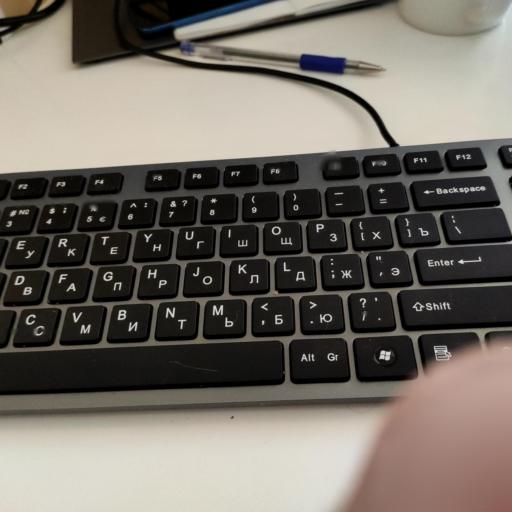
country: RU
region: Moskovskaya
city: Konstantinovo
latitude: 56.6335
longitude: 38.0112
